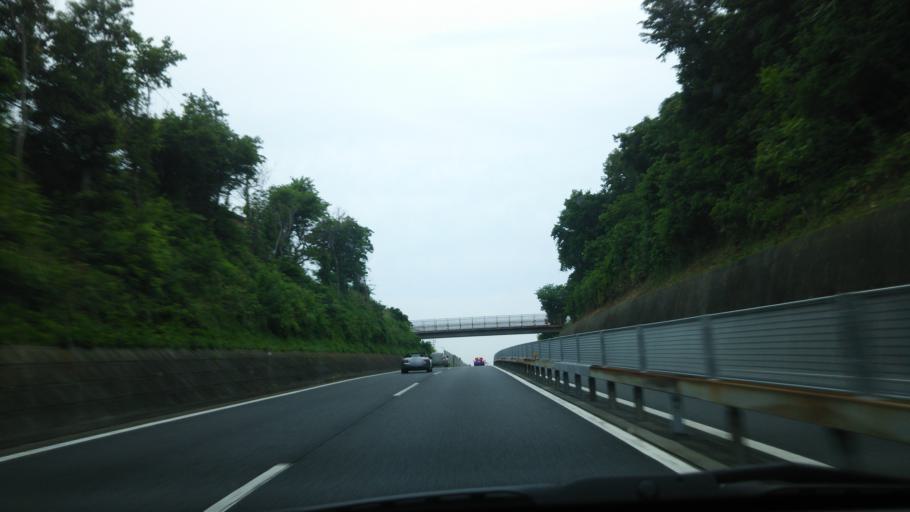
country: JP
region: Kanagawa
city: Isehara
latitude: 35.3509
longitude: 139.2983
